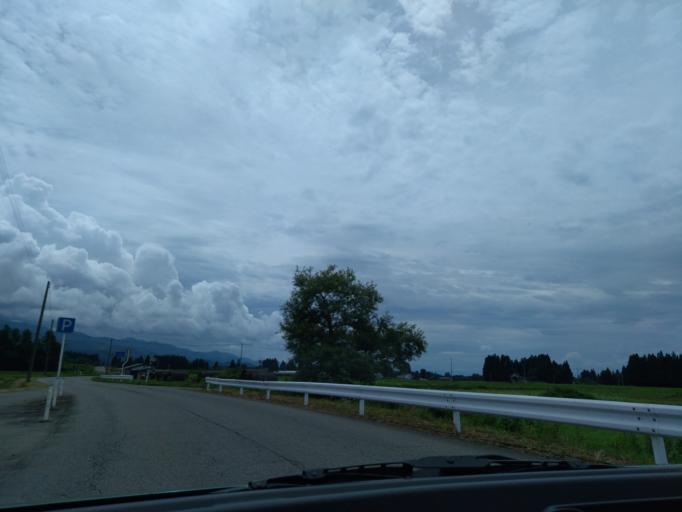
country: JP
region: Akita
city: Kakunodatemachi
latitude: 39.5333
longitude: 140.6409
